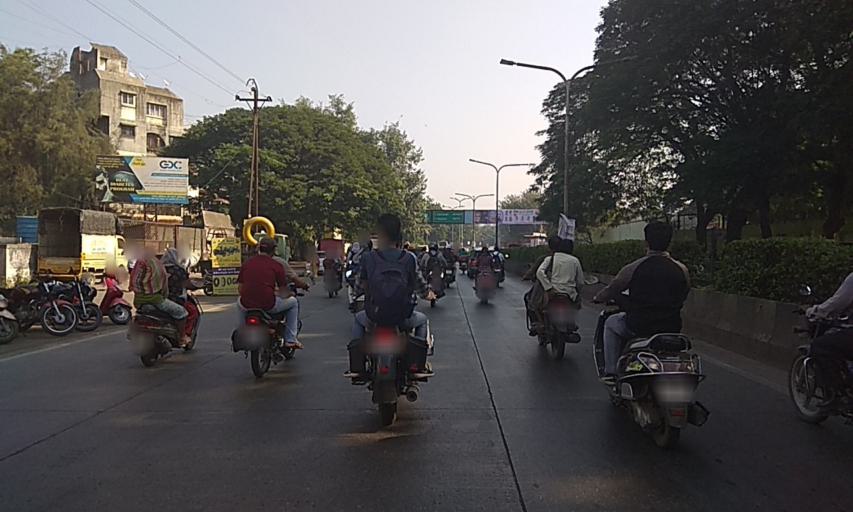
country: IN
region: Maharashtra
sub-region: Pune Division
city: Pune
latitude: 18.4980
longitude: 73.8409
